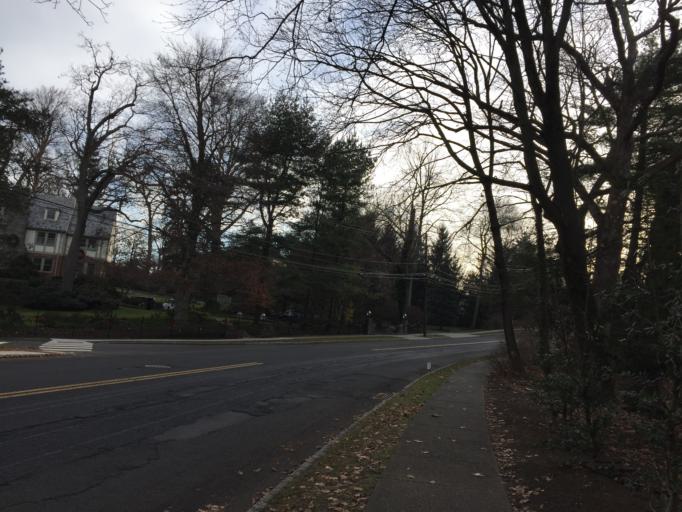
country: US
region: New Jersey
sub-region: Union County
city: Summit
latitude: 40.7185
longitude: -74.3508
